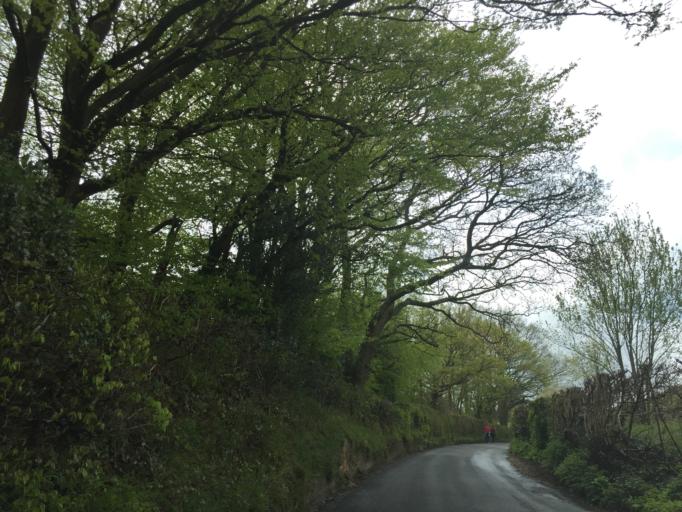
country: GB
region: England
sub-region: East Sussex
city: Heathfield
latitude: 51.0168
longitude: 0.2834
